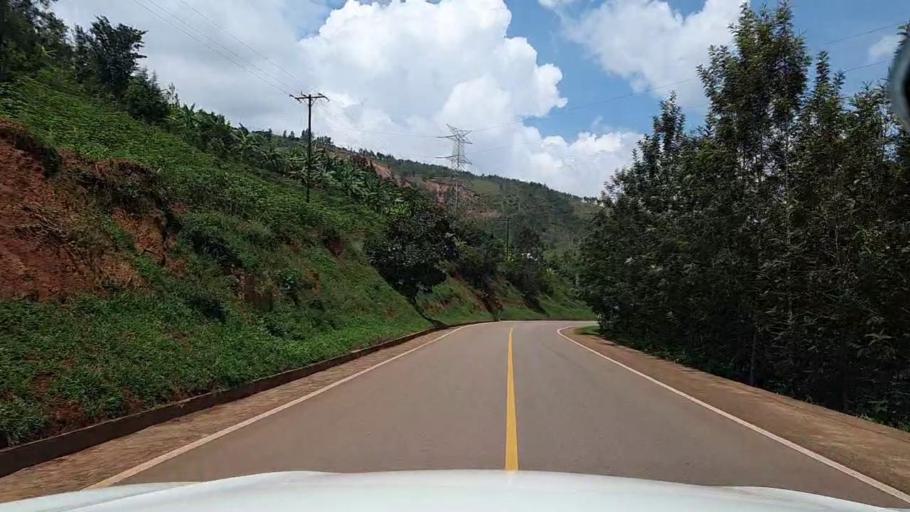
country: RW
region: Kigali
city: Kigali
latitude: -1.8362
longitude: 30.0807
